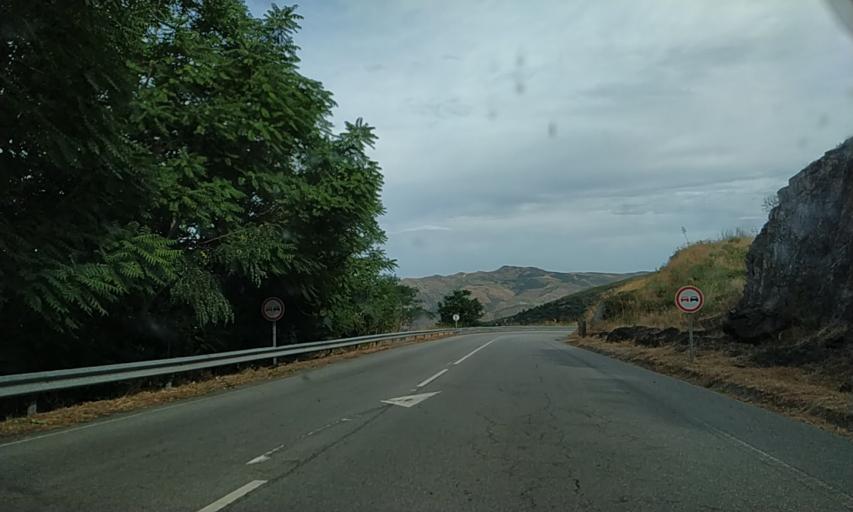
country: PT
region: Viseu
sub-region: Sao Joao da Pesqueira
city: Sao Joao da Pesqueira
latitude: 41.1355
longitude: -7.3990
